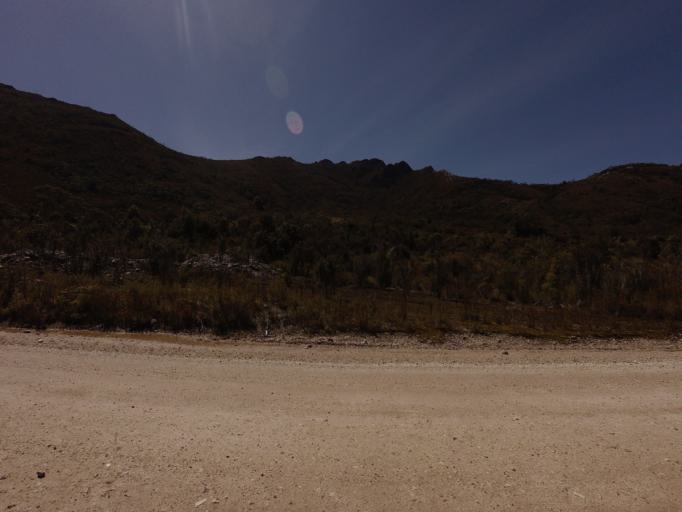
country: AU
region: Tasmania
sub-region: Huon Valley
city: Geeveston
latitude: -42.9362
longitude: 146.3472
